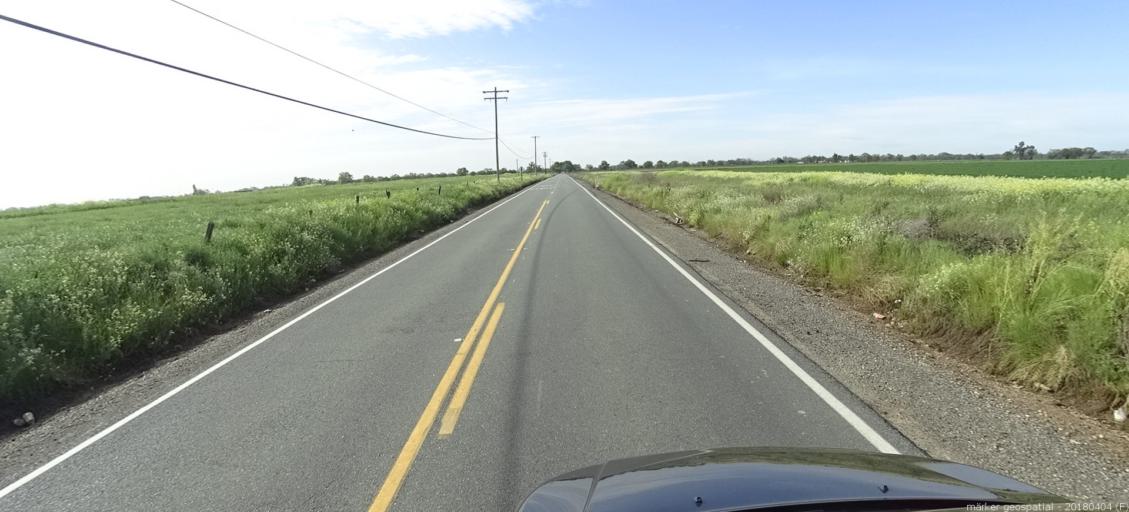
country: US
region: California
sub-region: Sacramento County
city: Herald
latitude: 38.2623
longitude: -121.2267
